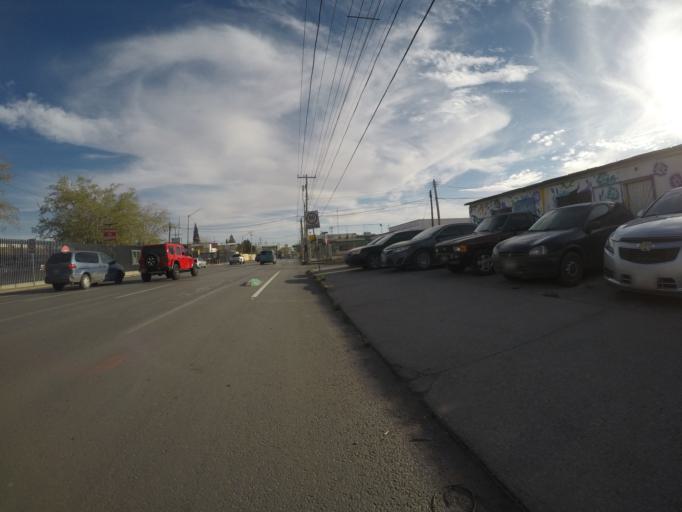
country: MX
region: Chihuahua
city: Ciudad Juarez
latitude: 31.7448
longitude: -106.4489
